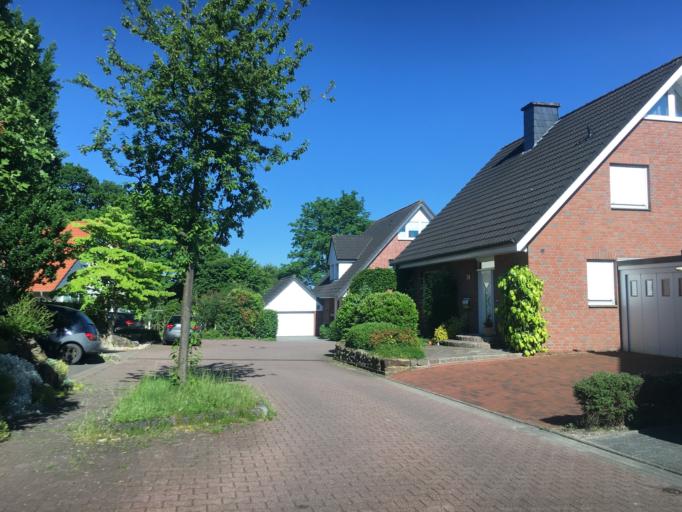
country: DE
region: North Rhine-Westphalia
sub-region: Regierungsbezirk Munster
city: Altenberge
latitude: 52.0467
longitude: 7.4777
